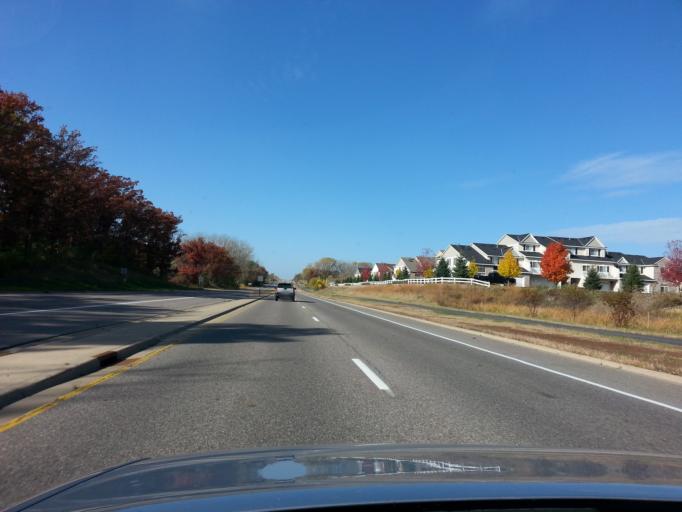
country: US
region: Minnesota
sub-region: Dakota County
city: Lakeville
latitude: 44.6814
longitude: -93.2995
